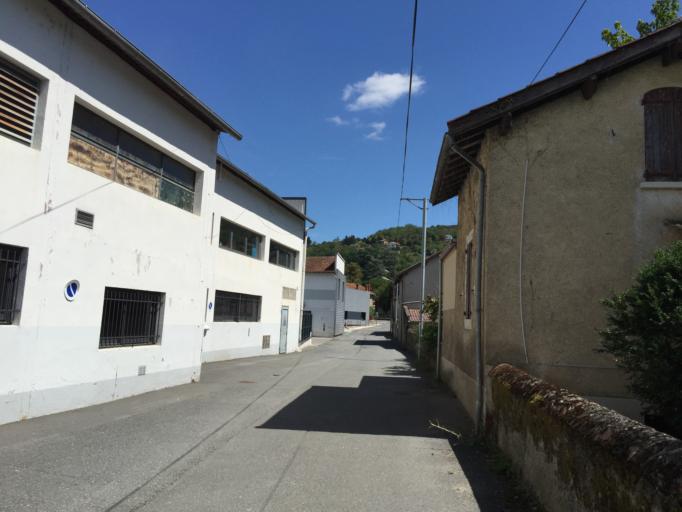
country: FR
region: Midi-Pyrenees
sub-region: Departement de l'Aveyron
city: Villefranche-de-Rouergue
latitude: 44.3450
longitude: 2.0305
